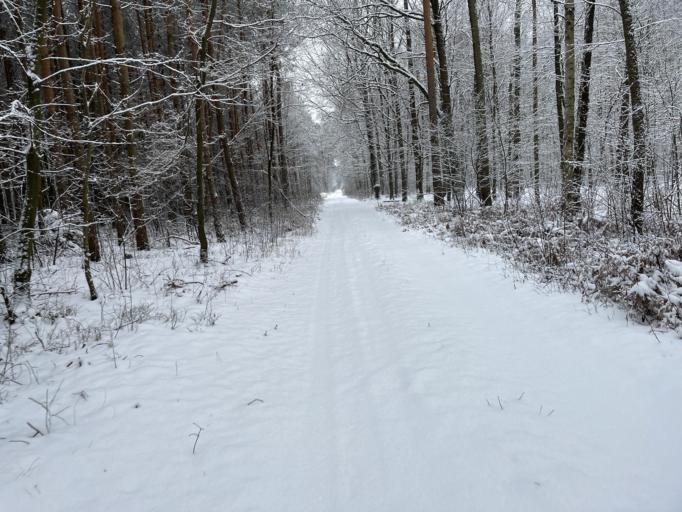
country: PL
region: Masovian Voivodeship
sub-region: Powiat zyrardowski
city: Mrozy
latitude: 52.0366
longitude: 20.2731
